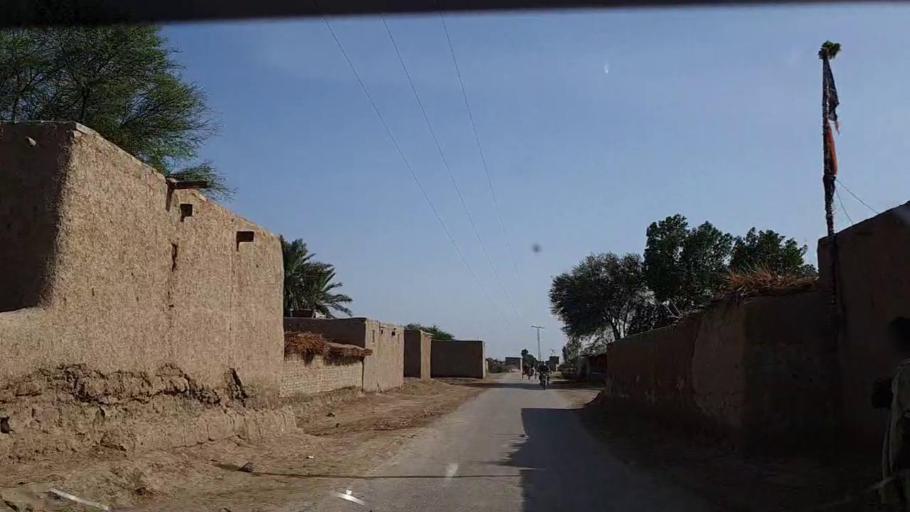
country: PK
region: Sindh
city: Phulji
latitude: 26.9956
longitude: 67.6657
